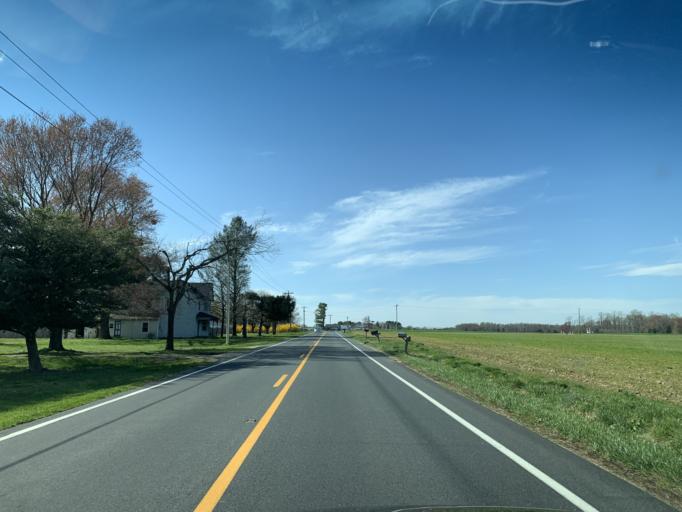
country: US
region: Delaware
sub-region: Kent County
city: Riverview
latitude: 39.0125
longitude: -75.5315
